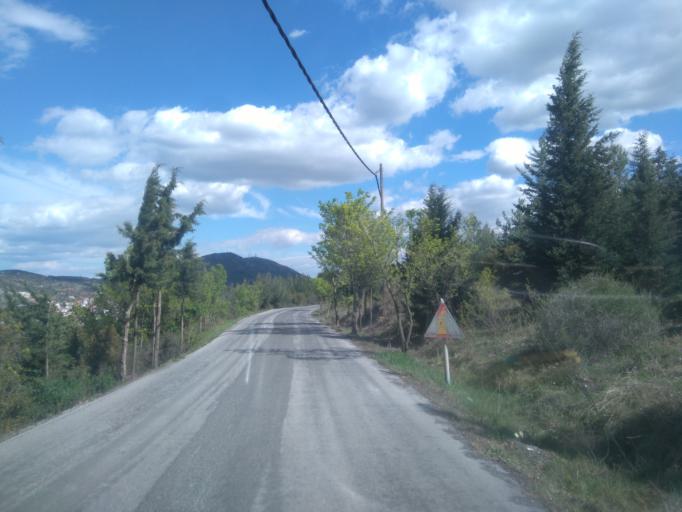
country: GR
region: Central Macedonia
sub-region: Nomos Thessalonikis
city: Pefka
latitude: 40.6421
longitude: 23.0042
